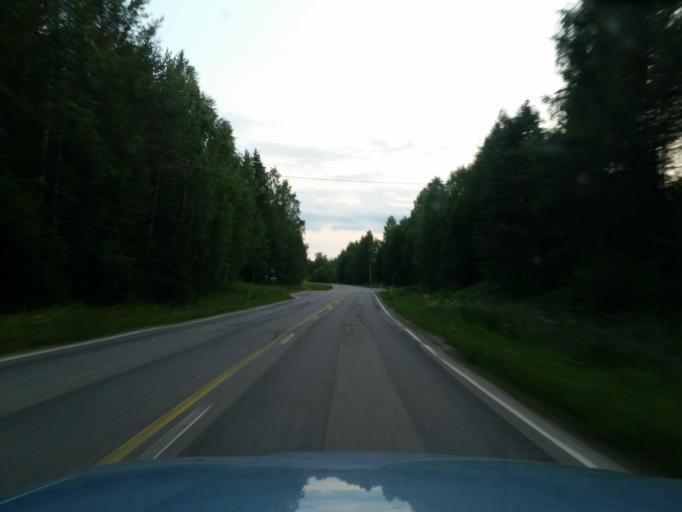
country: FI
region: Southern Savonia
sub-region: Savonlinna
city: Sulkava
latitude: 61.8320
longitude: 28.4521
